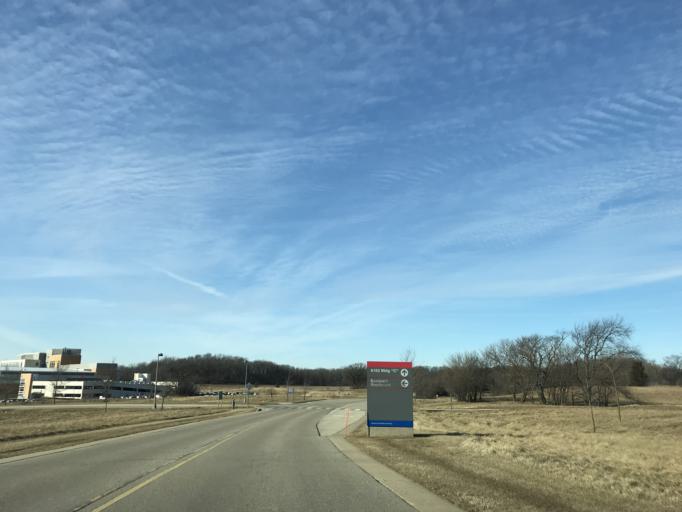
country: US
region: Wisconsin
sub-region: Dane County
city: Windsor
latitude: 43.1543
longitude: -89.2952
